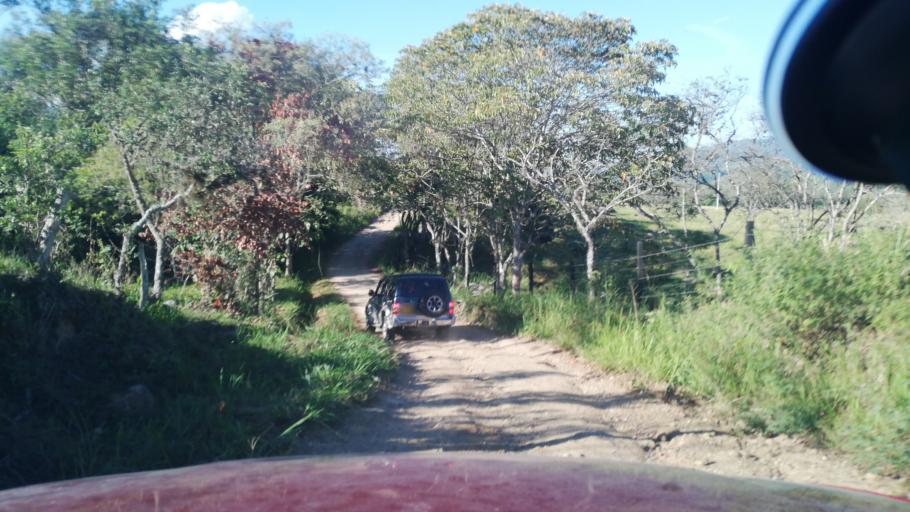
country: CO
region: Cundinamarca
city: Viani
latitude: 4.8191
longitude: -74.6163
